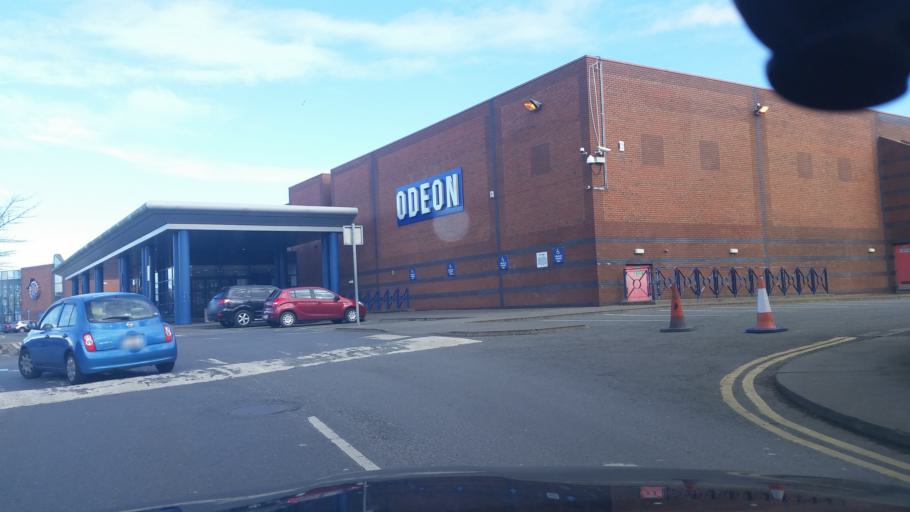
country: IE
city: Coolock
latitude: 53.3910
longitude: -6.1938
